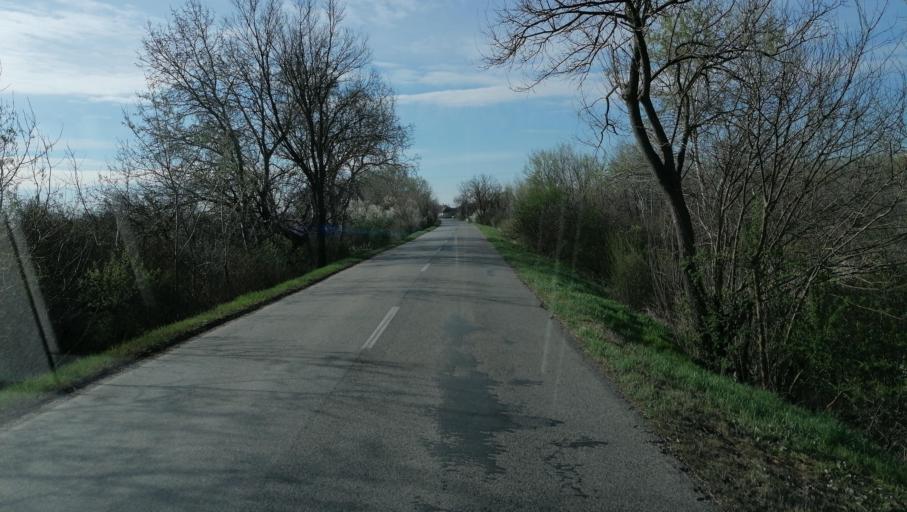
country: HU
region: Pest
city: Rackeve
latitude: 47.0990
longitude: 18.9272
